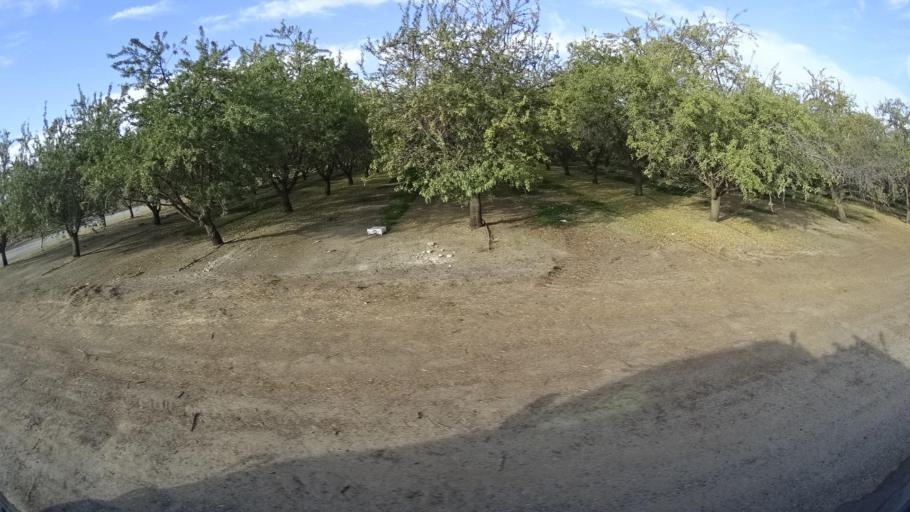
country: US
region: California
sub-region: Kern County
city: Delano
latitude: 35.7708
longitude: -119.2053
